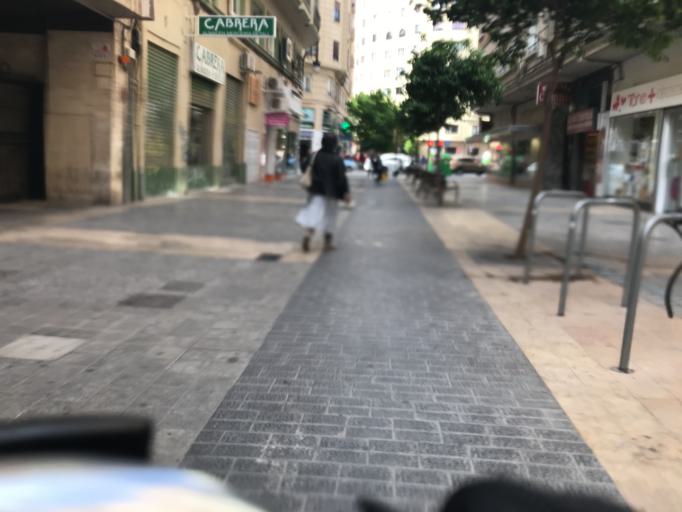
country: ES
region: Valencia
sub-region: Provincia de Valencia
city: Valencia
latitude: 39.4716
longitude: -0.3787
